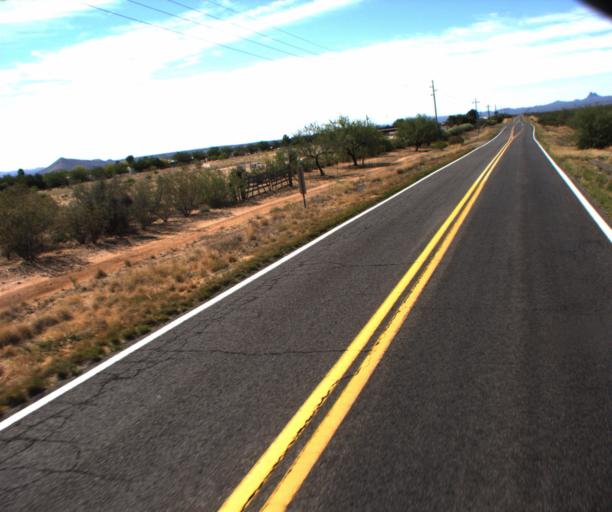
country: US
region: Arizona
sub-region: Yavapai County
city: Congress
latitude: 34.1076
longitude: -112.8323
